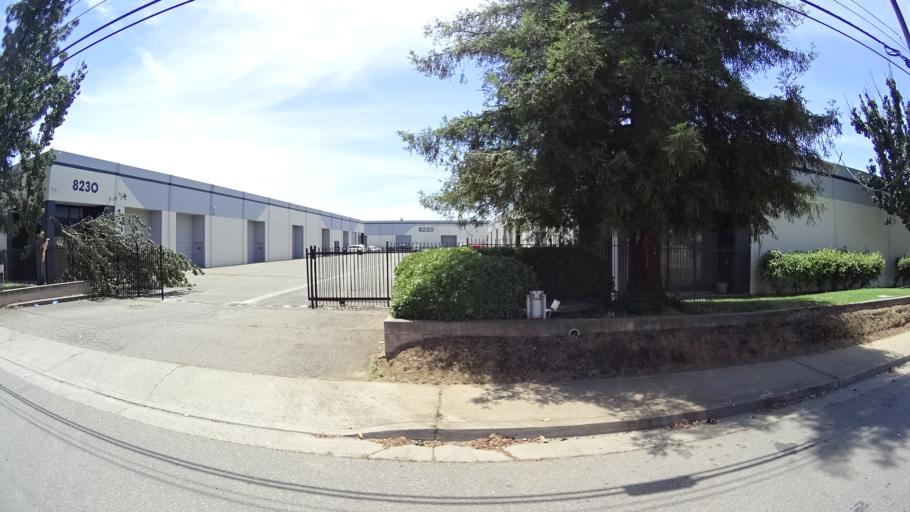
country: US
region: California
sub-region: Sacramento County
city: Florin
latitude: 38.5355
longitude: -121.4036
